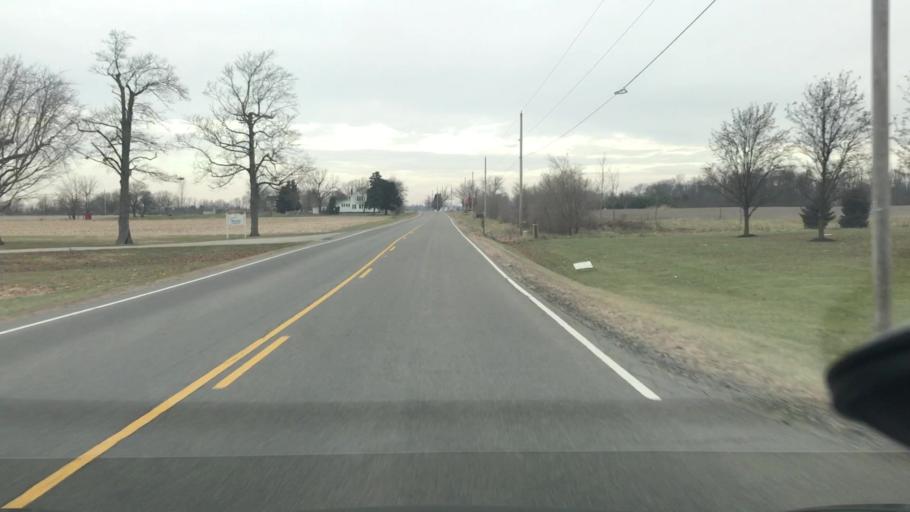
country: US
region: Ohio
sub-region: Madison County
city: London
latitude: 39.8331
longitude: -83.3730
